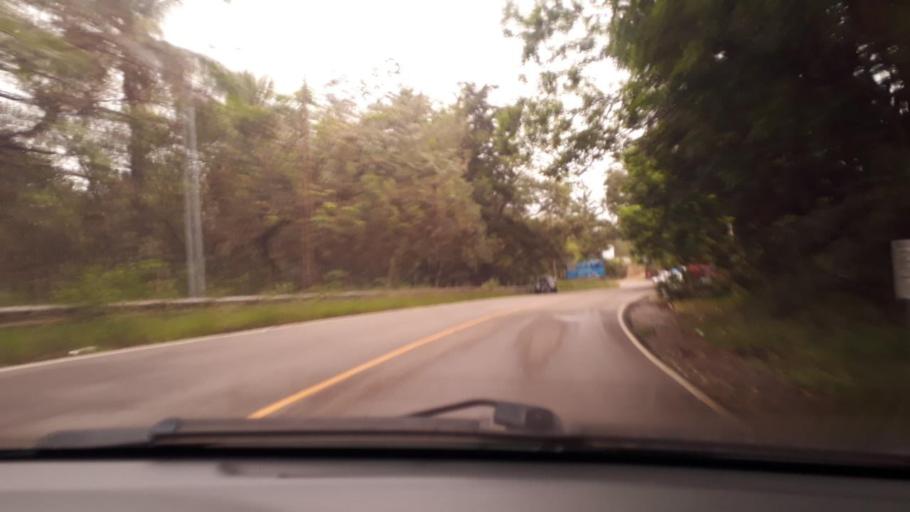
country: GT
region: Chiquimula
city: Esquipulas
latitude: 14.5456
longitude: -89.2856
